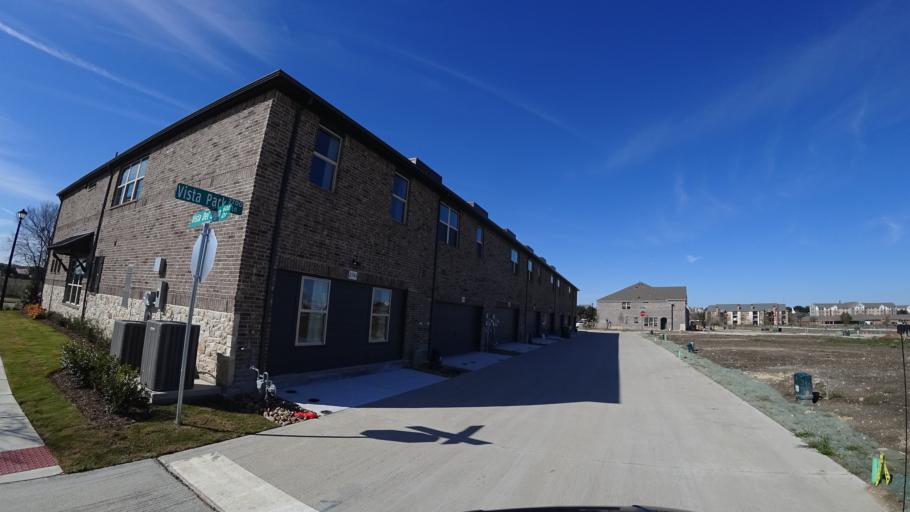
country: US
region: Texas
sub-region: Denton County
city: Lewisville
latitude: 32.9949
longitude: -96.9709
